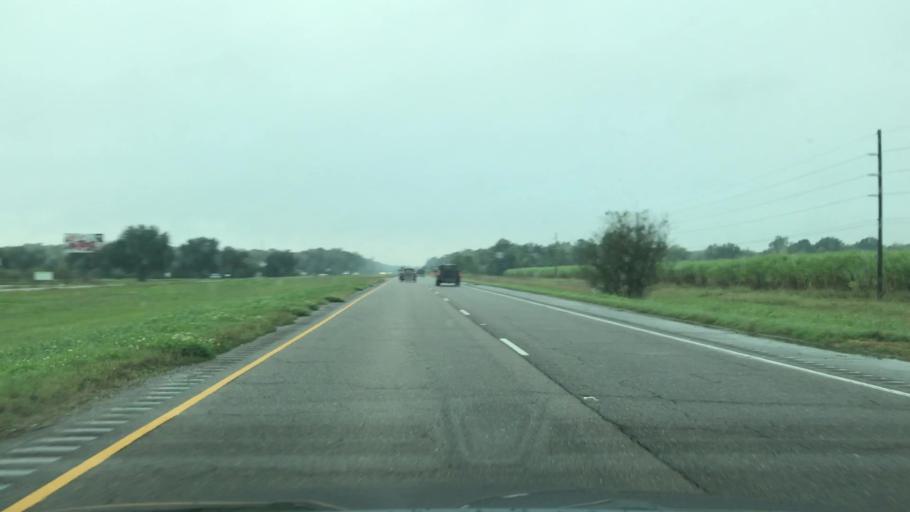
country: US
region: Louisiana
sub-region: Lafourche Parish
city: Raceland
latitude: 29.7409
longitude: -90.5572
